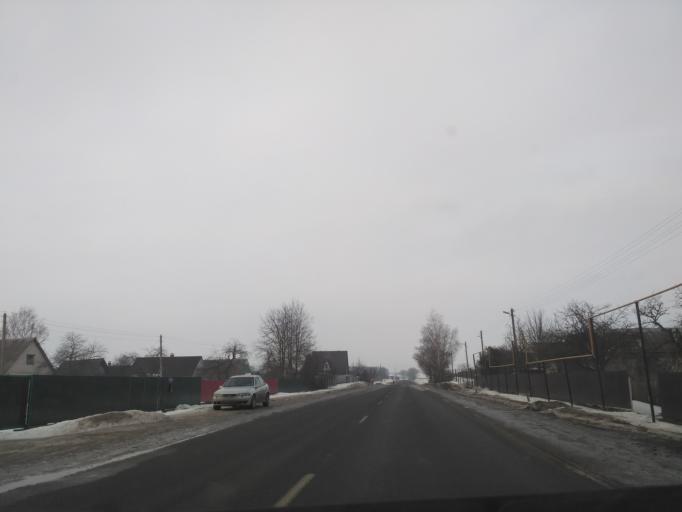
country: BY
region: Minsk
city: Horad Smalyavichy
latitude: 54.0270
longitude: 28.0633
